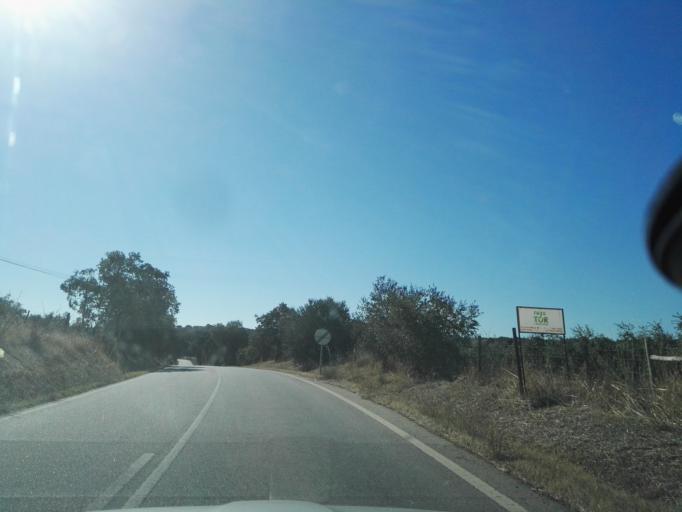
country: PT
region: Portalegre
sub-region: Elvas
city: Elvas
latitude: 38.9160
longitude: -7.1822
